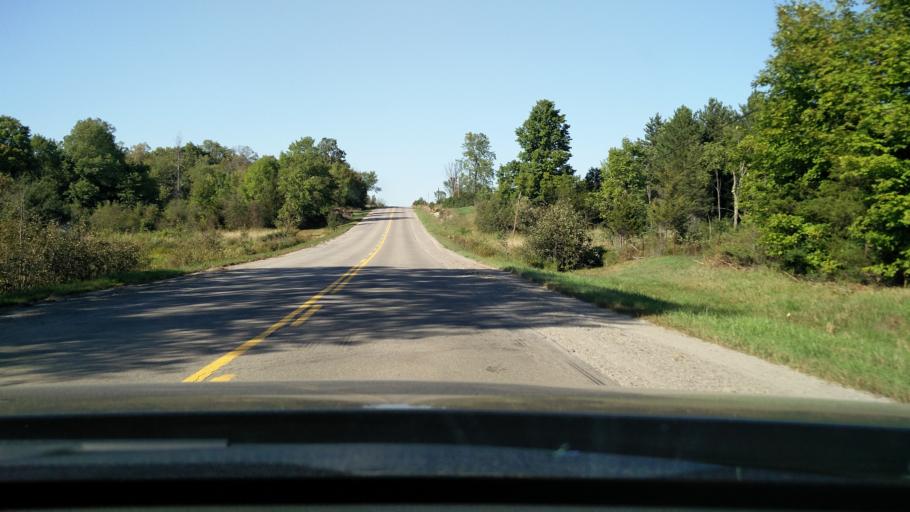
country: CA
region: Ontario
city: Perth
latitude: 44.7228
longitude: -76.3998
